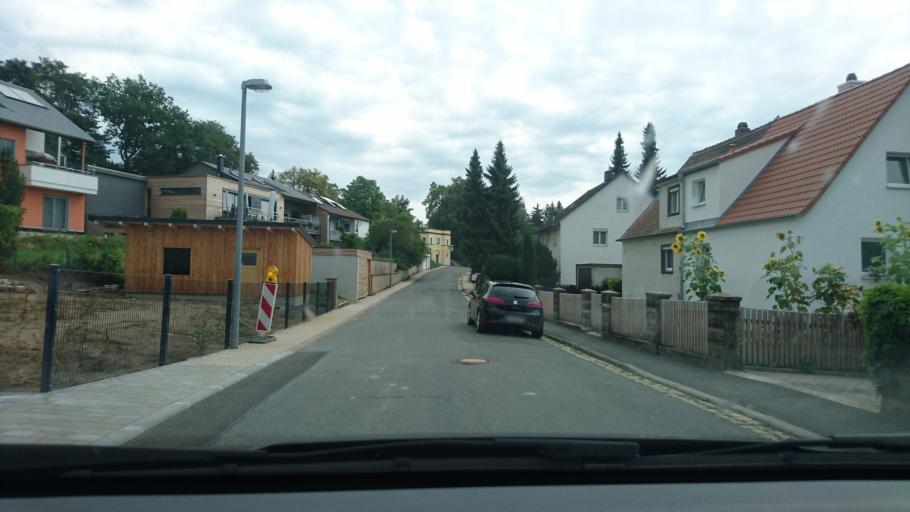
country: DE
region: Bavaria
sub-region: Upper Franconia
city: Bayreuth
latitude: 49.9632
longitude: 11.5843
